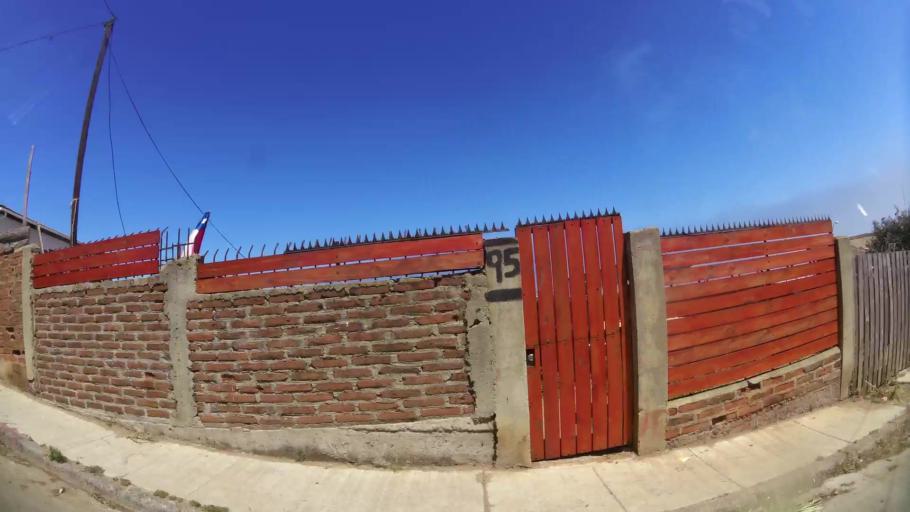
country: CL
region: Valparaiso
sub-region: Provincia de Valparaiso
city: Valparaiso
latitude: -33.0327
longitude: -71.6540
